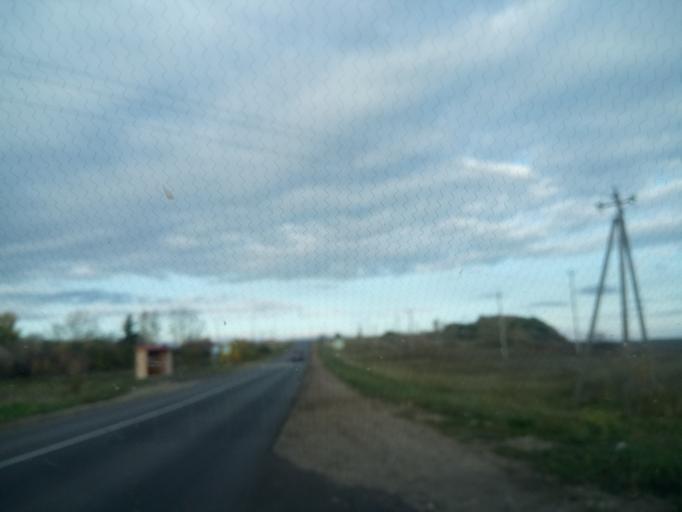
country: RU
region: Nizjnij Novgorod
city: Gagino
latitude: 55.2477
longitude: 45.0638
